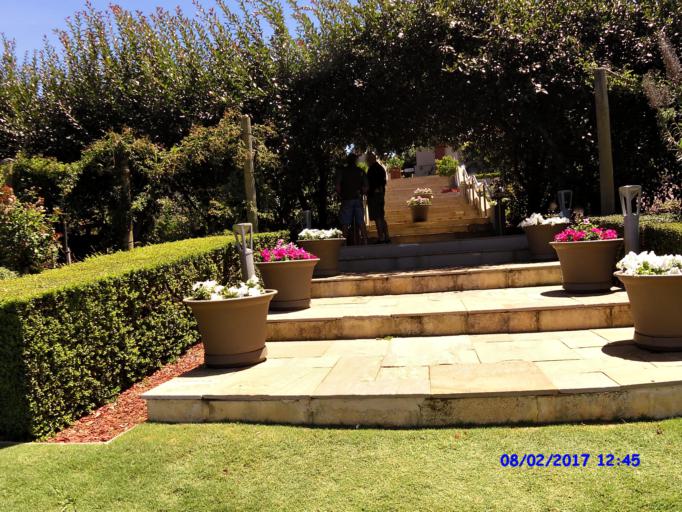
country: AU
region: Western Australia
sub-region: Kalamunda
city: Gooseberry Hill
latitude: -32.0254
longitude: 116.0729
